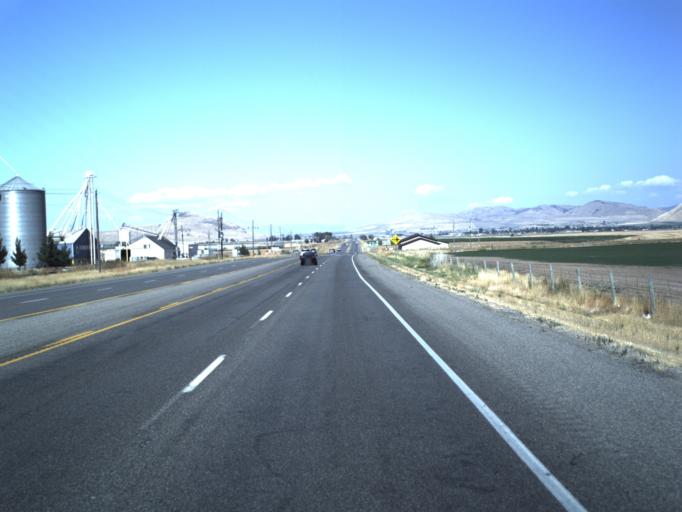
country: US
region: Utah
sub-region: Cache County
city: Lewiston
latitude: 41.9727
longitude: -111.8128
